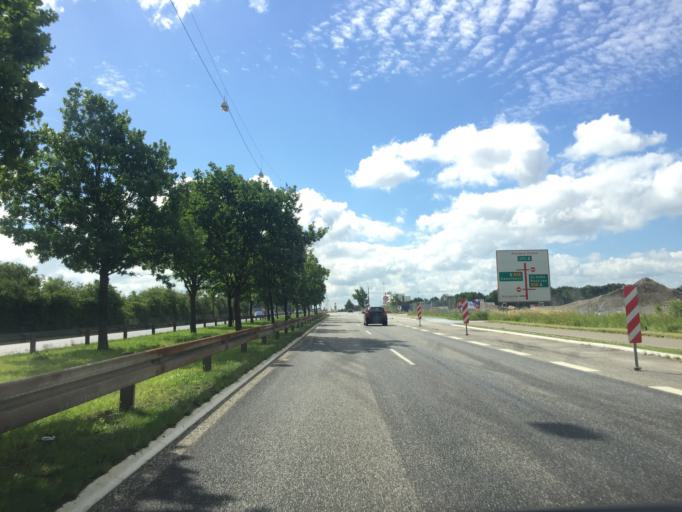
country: DK
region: Capital Region
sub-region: Hvidovre Kommune
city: Hvidovre
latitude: 55.6515
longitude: 12.4572
